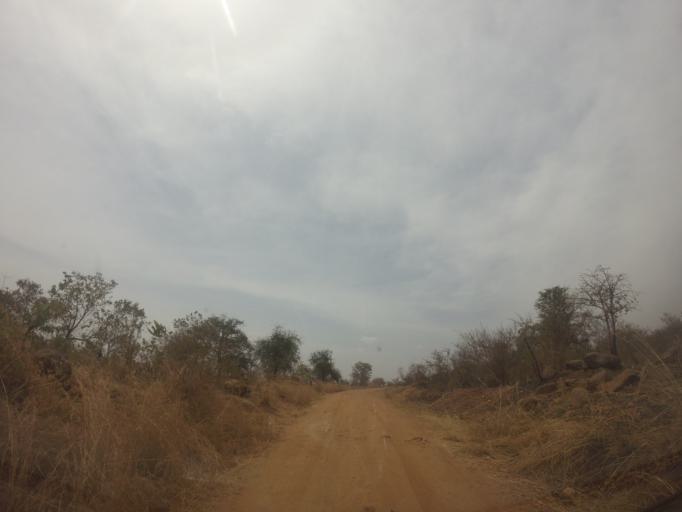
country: UG
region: Northern Region
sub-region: Nebbi District
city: Nebbi
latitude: 2.6339
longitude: 31.0317
